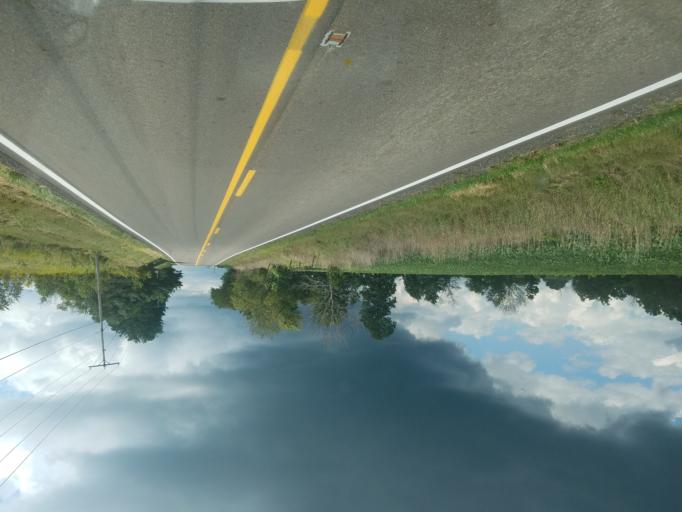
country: US
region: Ohio
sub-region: Huron County
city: Greenwich
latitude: 40.9158
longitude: -82.5098
